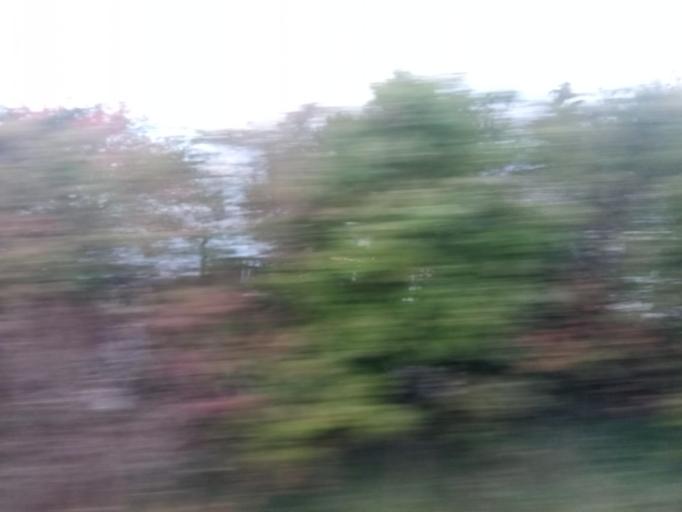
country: GB
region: Scotland
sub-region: Midlothian
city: Dalkeith
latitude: 55.8844
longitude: -3.0260
